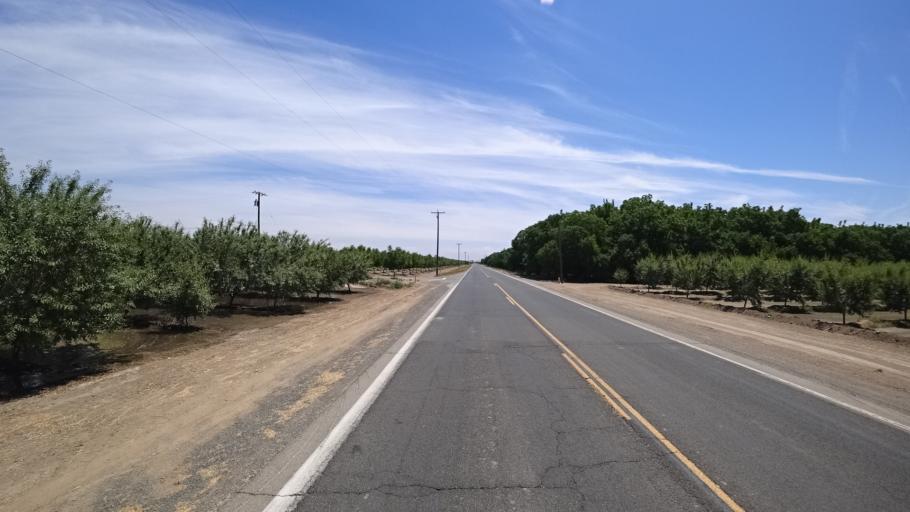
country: US
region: California
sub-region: Kings County
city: Lemoore
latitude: 36.3426
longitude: -119.7678
